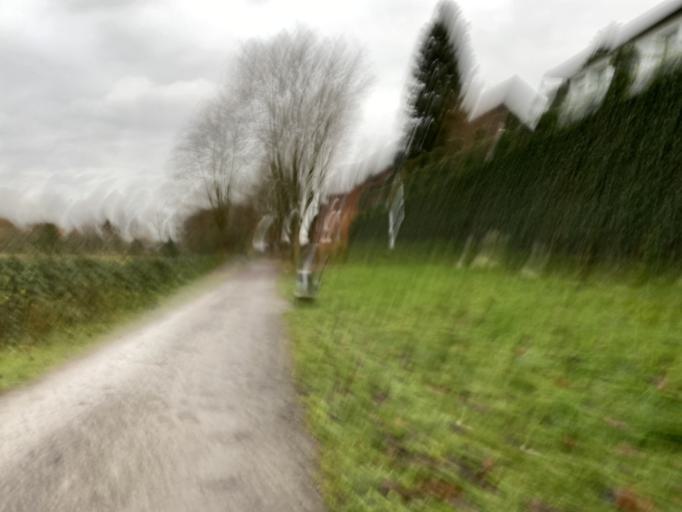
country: DE
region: North Rhine-Westphalia
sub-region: Regierungsbezirk Arnsberg
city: Hamm
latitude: 51.6773
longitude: 7.8411
